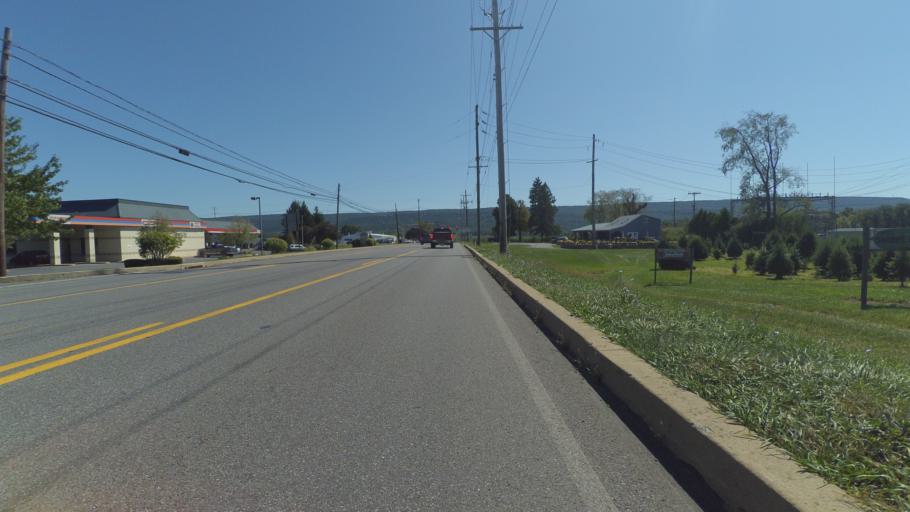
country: US
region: Pennsylvania
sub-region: Centre County
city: Pine Grove Mills
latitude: 40.7609
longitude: -77.8790
